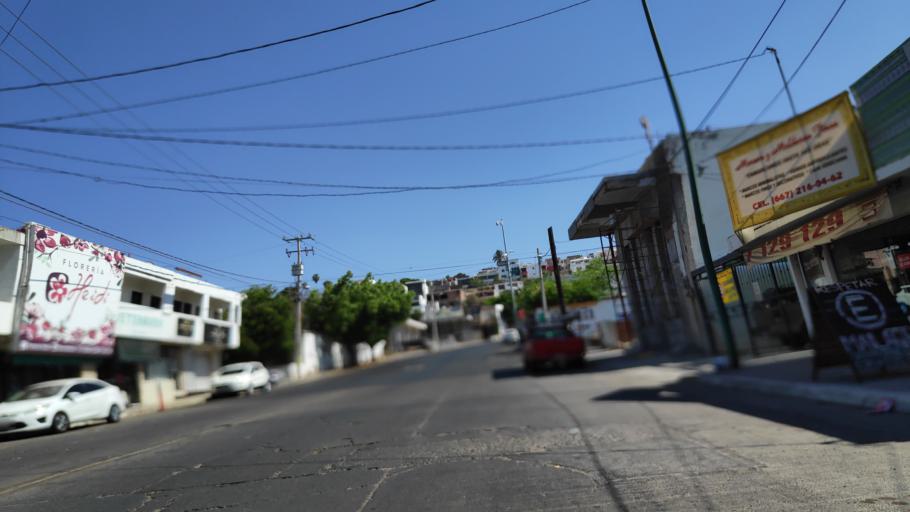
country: MX
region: Sinaloa
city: Culiacan
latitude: 24.7867
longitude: -107.4005
